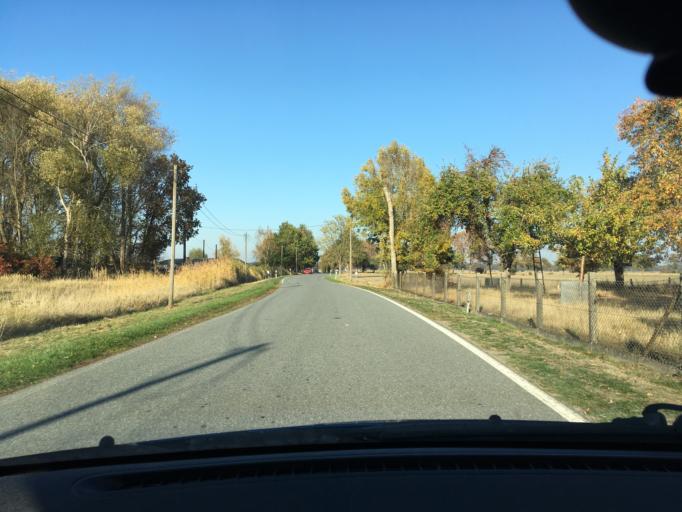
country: DE
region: Lower Saxony
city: Hitzacker
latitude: 53.1704
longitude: 11.0369
